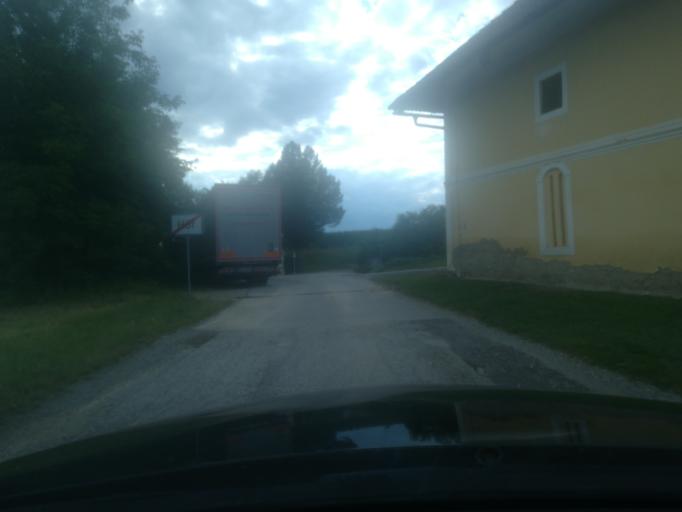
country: AT
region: Upper Austria
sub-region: Politischer Bezirk Urfahr-Umgebung
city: Ottensheim
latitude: 48.3218
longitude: 14.1826
